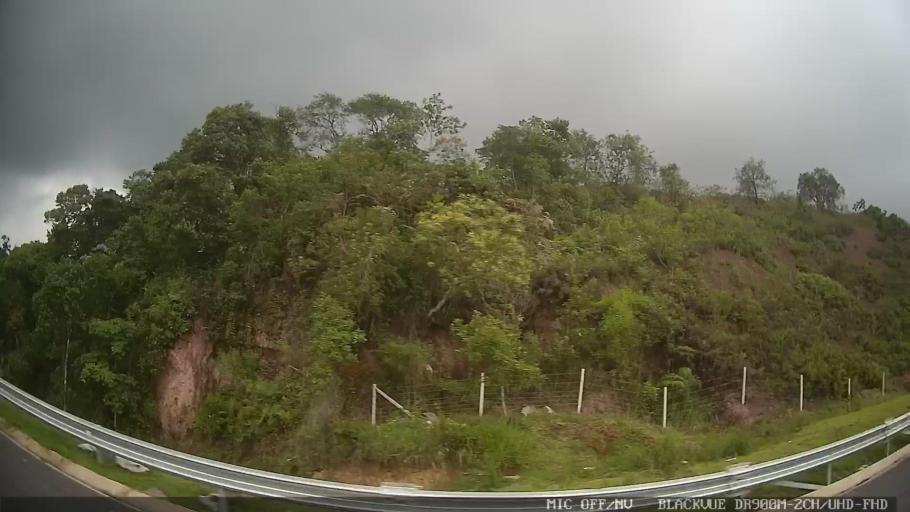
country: BR
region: Sao Paulo
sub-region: Aruja
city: Aruja
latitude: -23.4216
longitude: -46.2830
